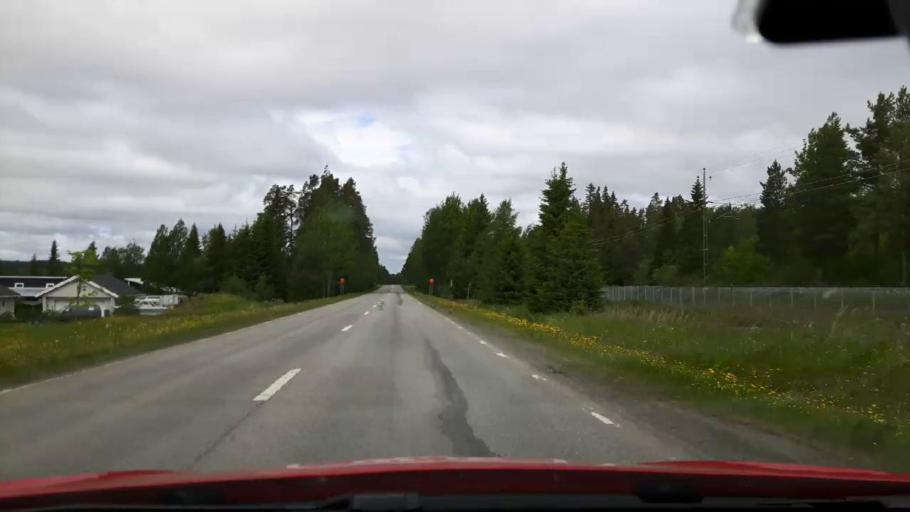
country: SE
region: Jaemtland
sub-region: Krokoms Kommun
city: Krokom
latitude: 63.2932
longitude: 14.4903
